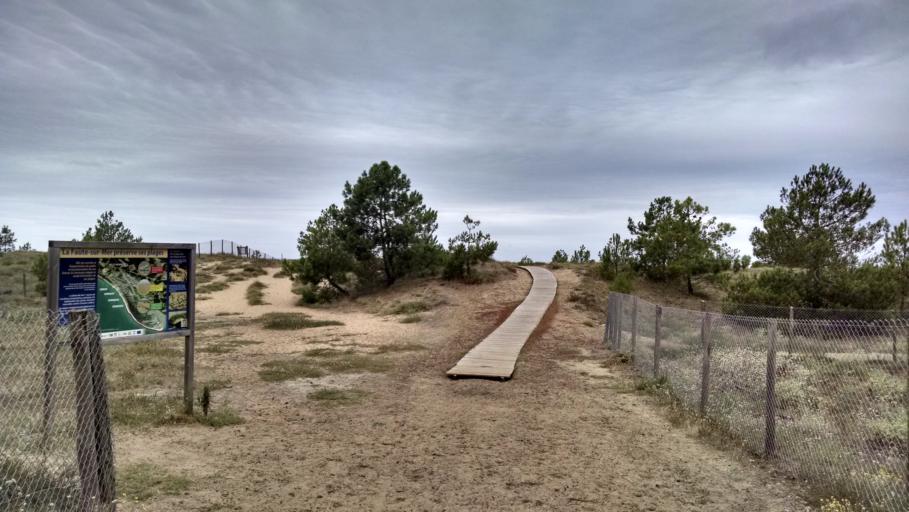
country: FR
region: Poitou-Charentes
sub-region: Departement de la Charente-Maritime
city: Saint-Martin-de-Re
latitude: 46.3133
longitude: -1.3133
